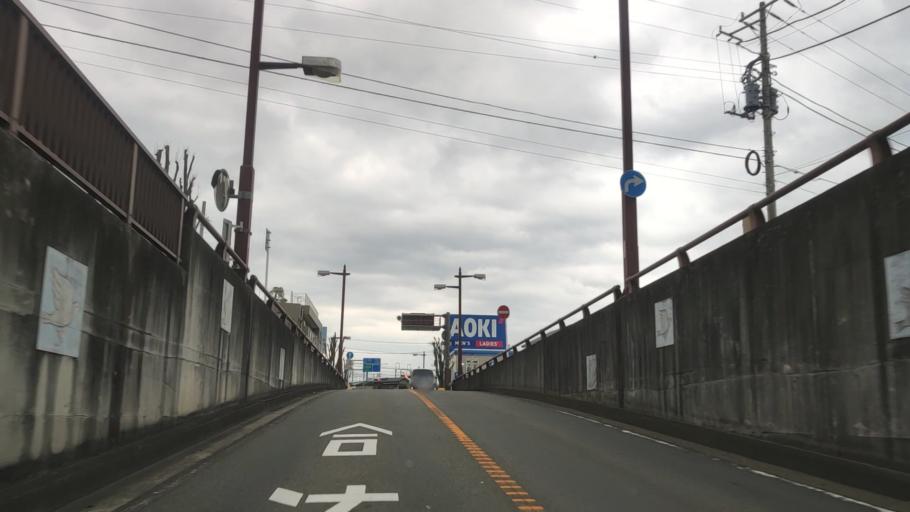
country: JP
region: Kanagawa
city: Odawara
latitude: 35.2636
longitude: 139.1585
